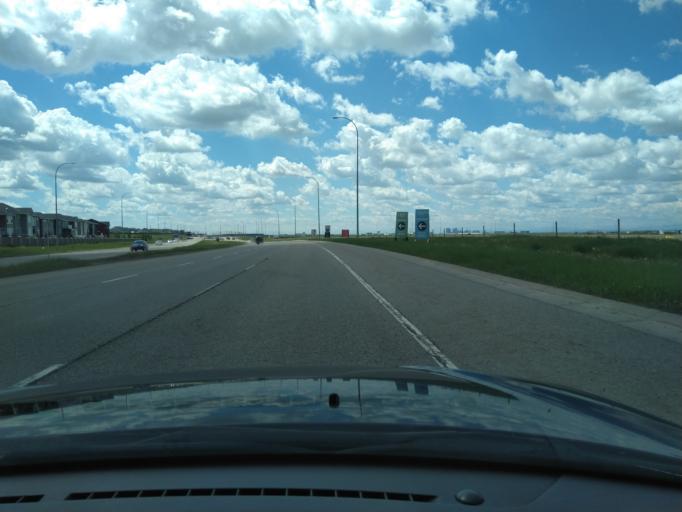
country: CA
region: Alberta
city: Airdrie
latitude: 51.1699
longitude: -113.9700
